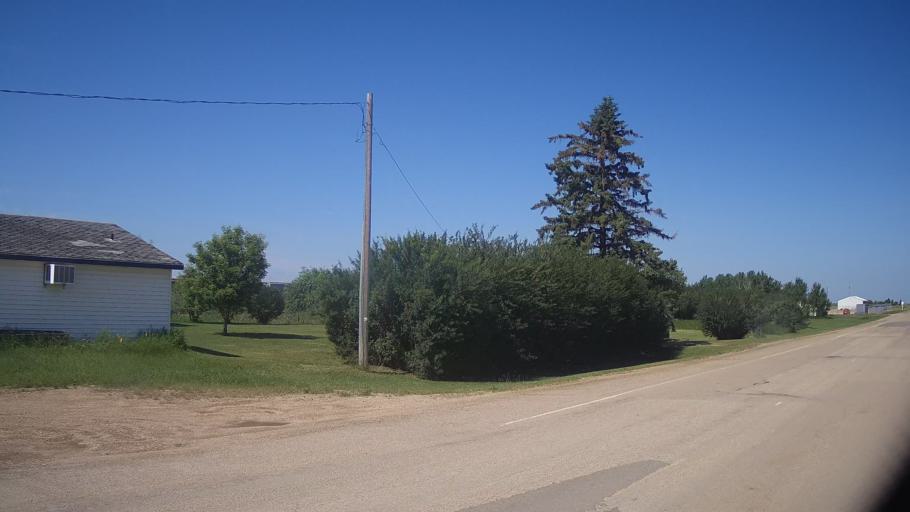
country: CA
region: Saskatchewan
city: Saskatoon
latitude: 51.8940
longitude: -106.0587
